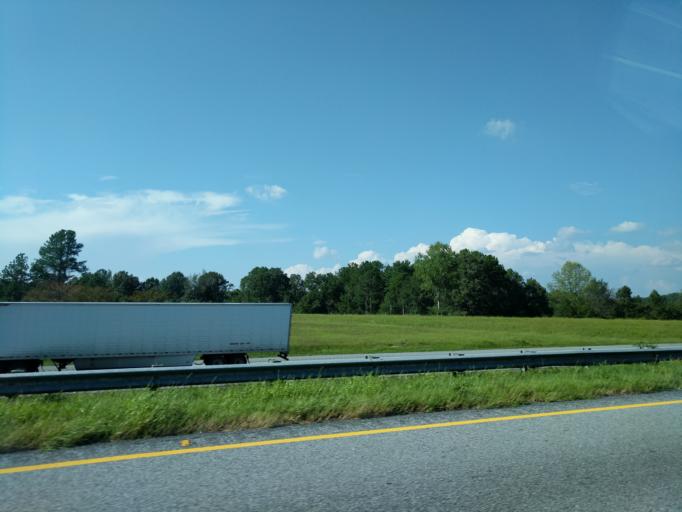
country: US
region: Georgia
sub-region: Franklin County
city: Gumlog
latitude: 34.4903
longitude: -83.0212
